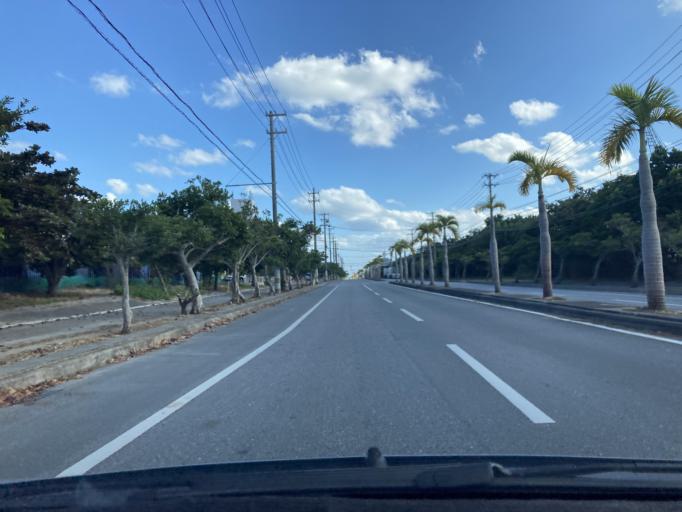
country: JP
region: Okinawa
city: Katsuren-haebaru
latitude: 26.3348
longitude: 127.8504
